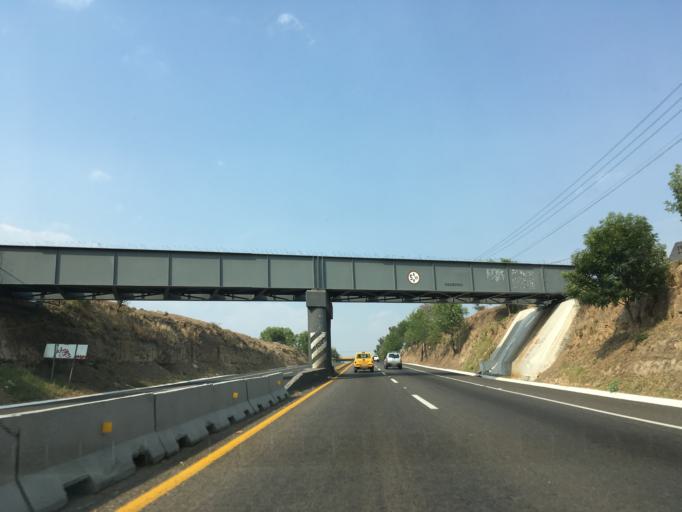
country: MX
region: Michoacan
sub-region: Morelia
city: Morelos
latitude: 19.6615
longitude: -101.2345
